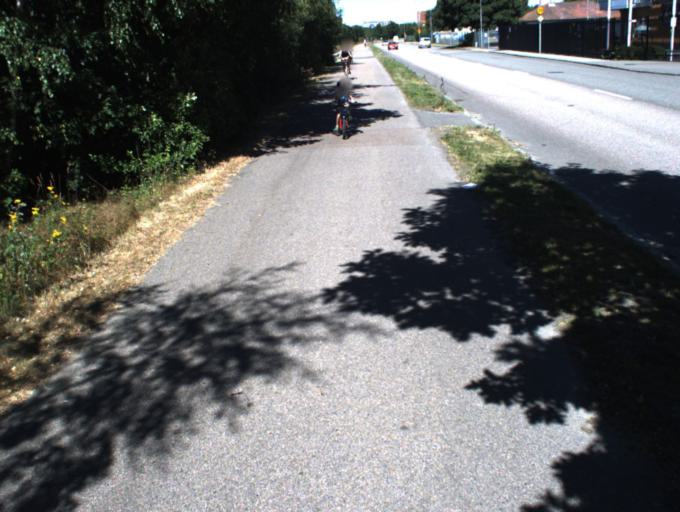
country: SE
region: Skane
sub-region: Helsingborg
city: Helsingborg
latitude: 56.0079
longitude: 12.7240
